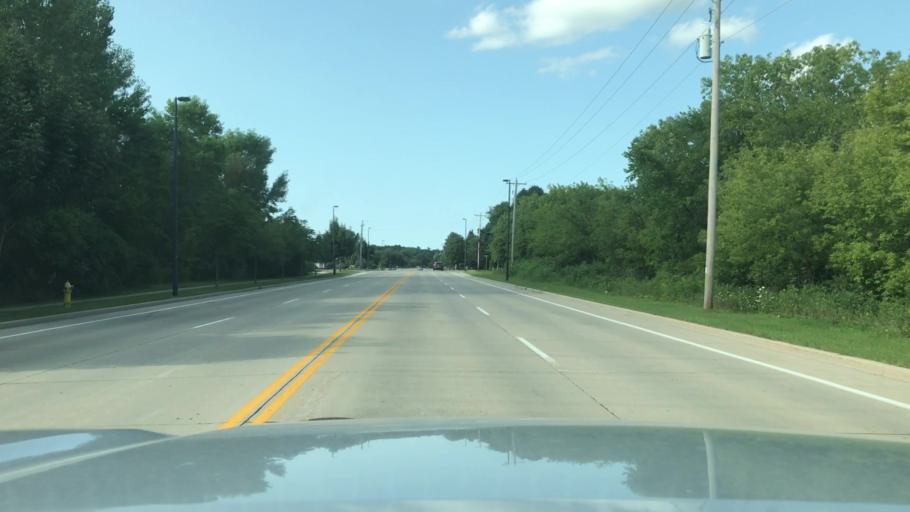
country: US
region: Wisconsin
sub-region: Brown County
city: Bellevue
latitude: 44.4892
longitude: -87.9178
